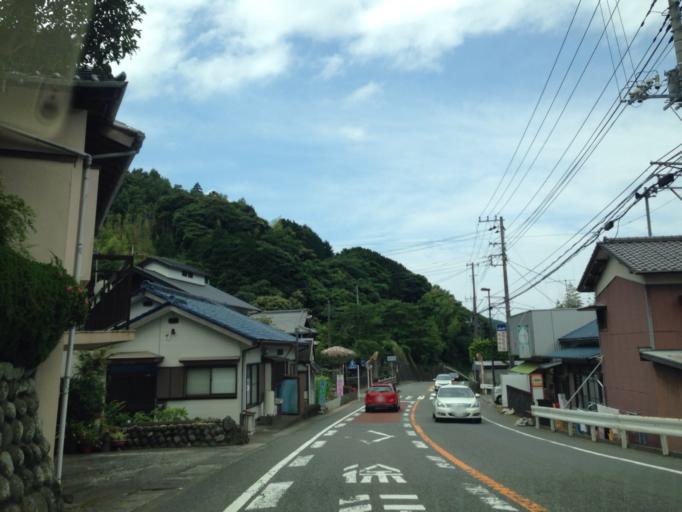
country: JP
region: Shizuoka
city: Heda
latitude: 34.9061
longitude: 138.8200
